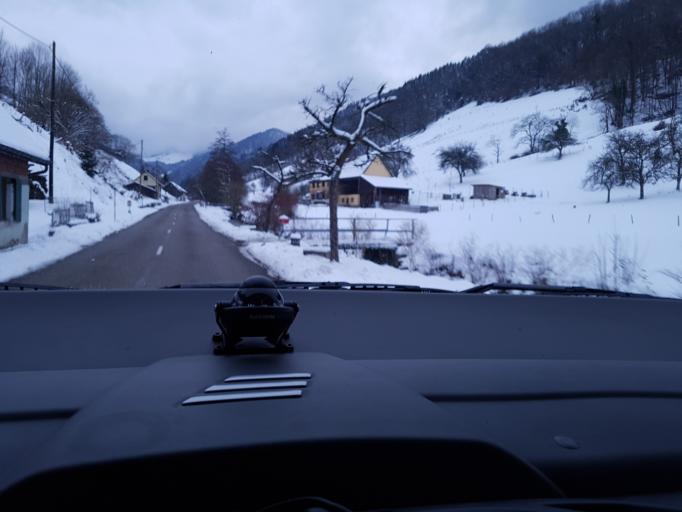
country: FR
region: Alsace
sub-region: Departement du Haut-Rhin
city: Sainte-Marie-aux-Mines
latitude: 48.2286
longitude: 7.1541
